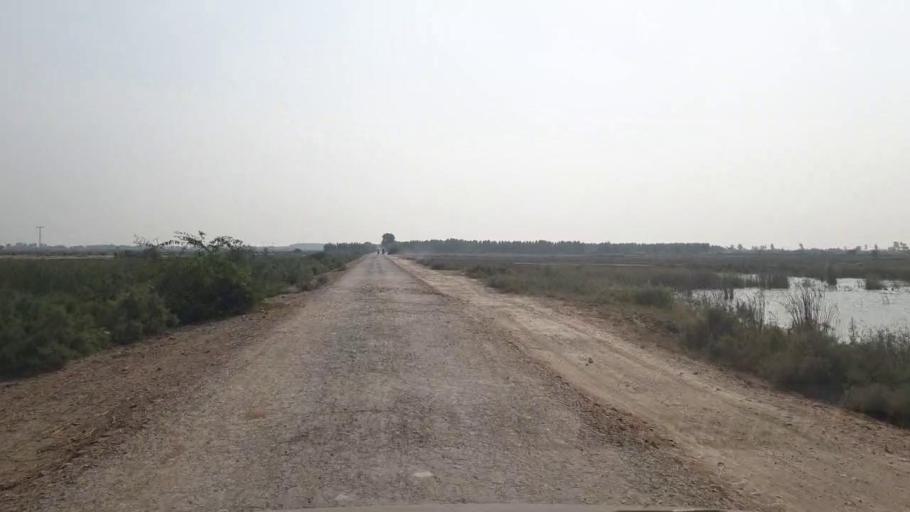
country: PK
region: Sindh
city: Tando Muhammad Khan
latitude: 25.0462
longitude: 68.3898
